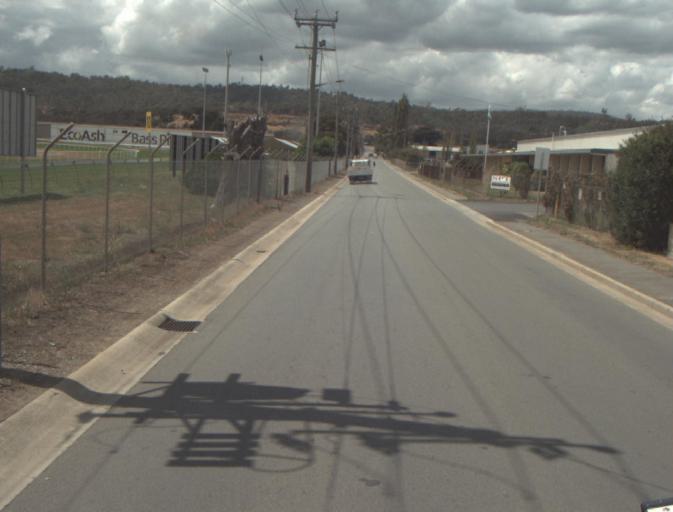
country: AU
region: Tasmania
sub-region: Launceston
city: Newnham
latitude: -41.4063
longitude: 147.1444
